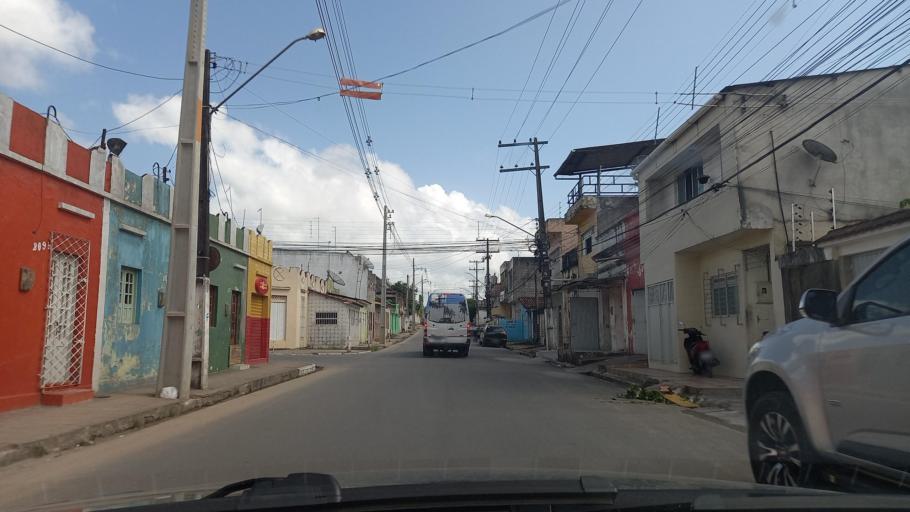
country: BR
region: Pernambuco
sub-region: Goiana
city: Goiana
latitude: -7.5644
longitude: -35.0010
